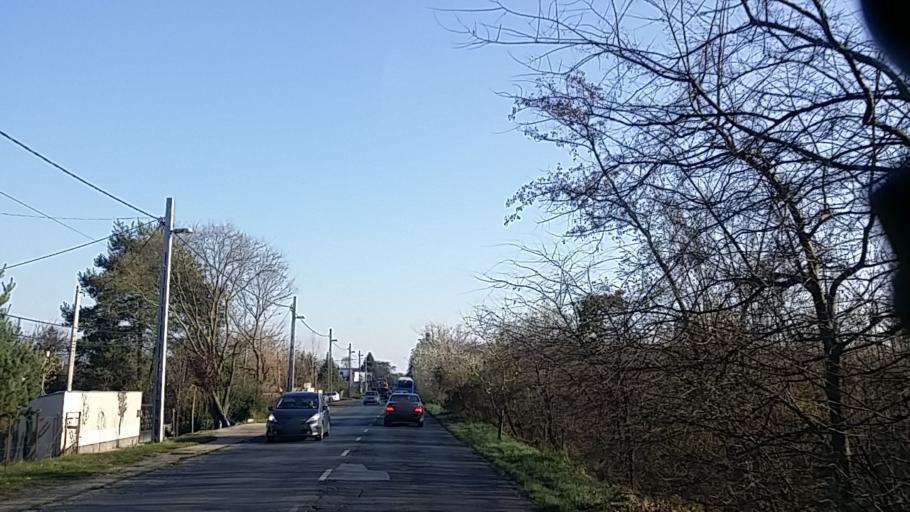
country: HU
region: Budapest
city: Budapest XVIII. keruelet
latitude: 47.4544
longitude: 19.2181
